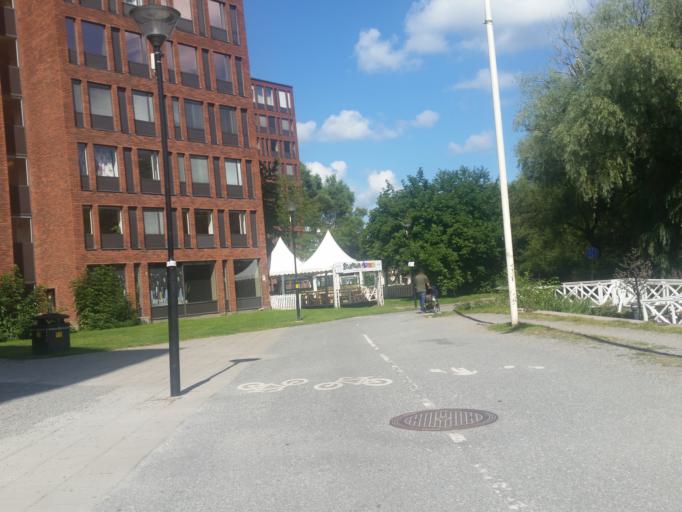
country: SE
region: Stockholm
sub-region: Stockholms Kommun
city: Stockholm
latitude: 59.3327
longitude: 18.0492
